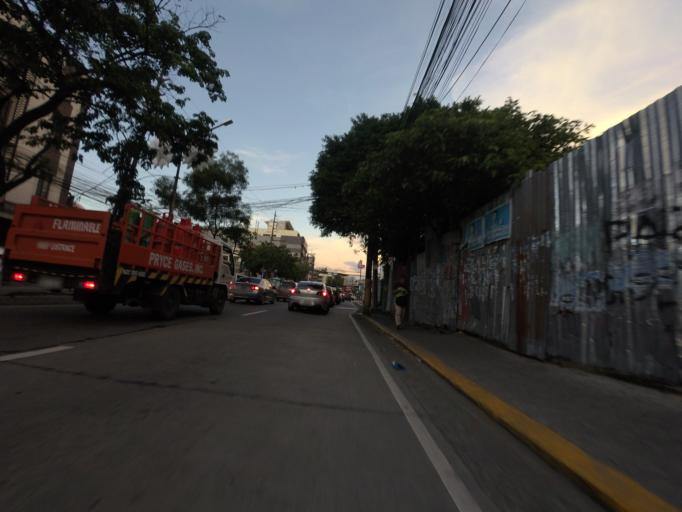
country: PH
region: Metro Manila
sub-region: City of Manila
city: Quiapo
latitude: 14.5985
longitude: 120.9901
